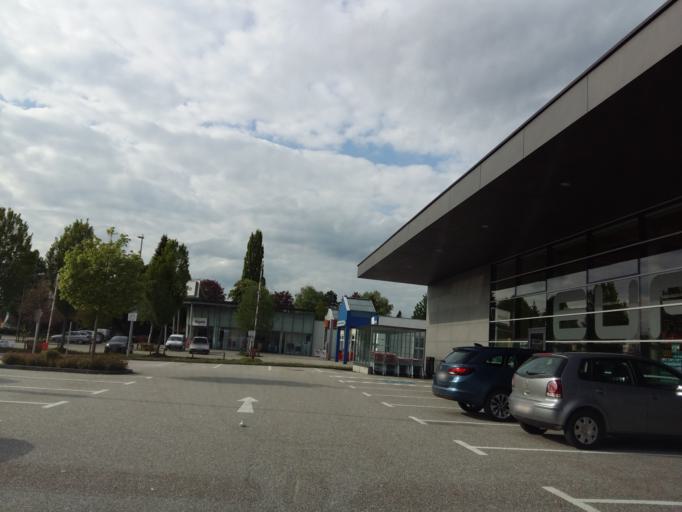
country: AT
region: Upper Austria
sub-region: Politischer Bezirk Scharding
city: Scharding
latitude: 48.4480
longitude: 13.4388
